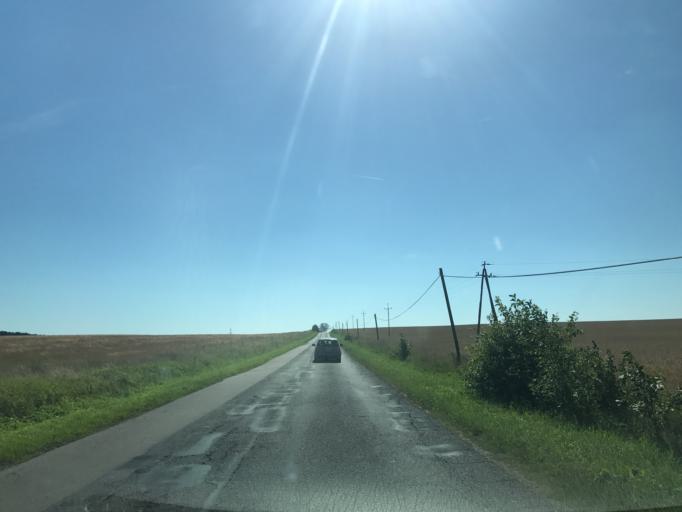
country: PL
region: Pomeranian Voivodeship
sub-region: Powiat bytowski
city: Czarna Dabrowka
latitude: 54.3646
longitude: 17.5135
